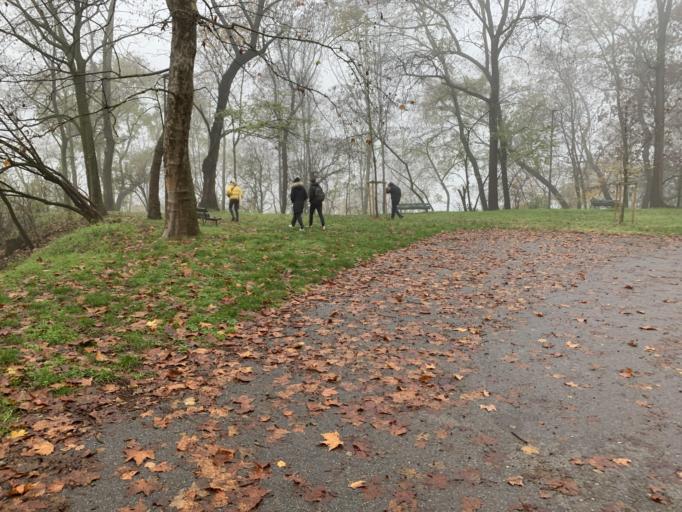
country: IT
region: Lombardy
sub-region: Citta metropolitana di Milano
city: Baranzate
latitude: 45.4884
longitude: 9.1338
